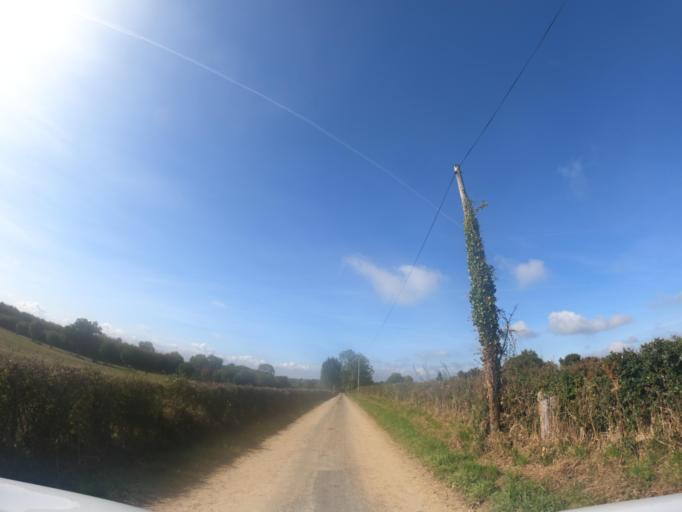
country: FR
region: Poitou-Charentes
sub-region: Departement des Deux-Sevres
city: Courlay
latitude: 46.7878
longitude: -0.5662
